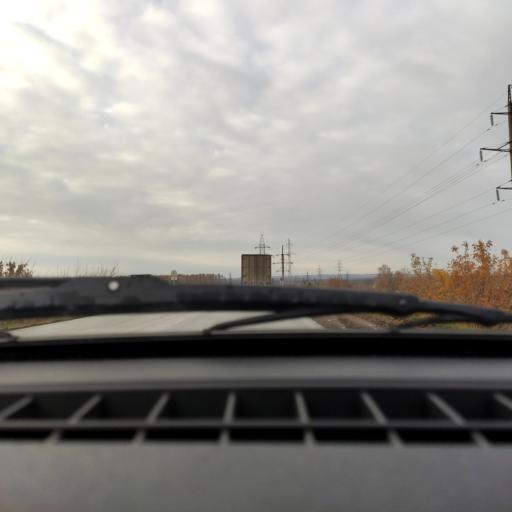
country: RU
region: Bashkortostan
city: Iglino
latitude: 54.7556
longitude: 56.2557
